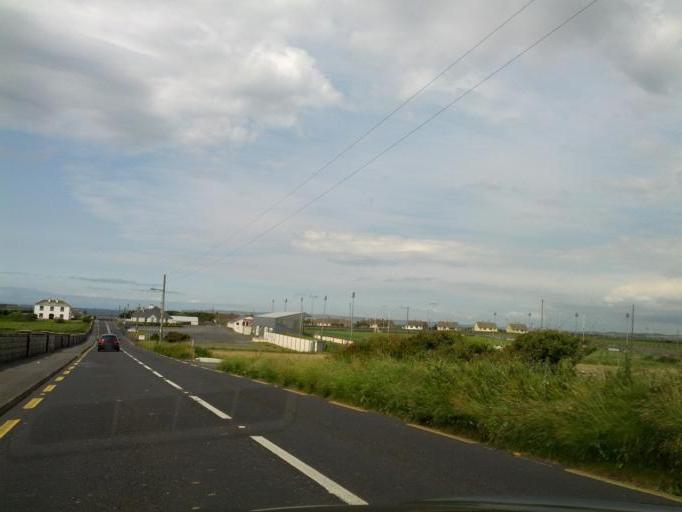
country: IE
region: Munster
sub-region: An Clar
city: Kilrush
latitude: 52.8123
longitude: -9.4550
